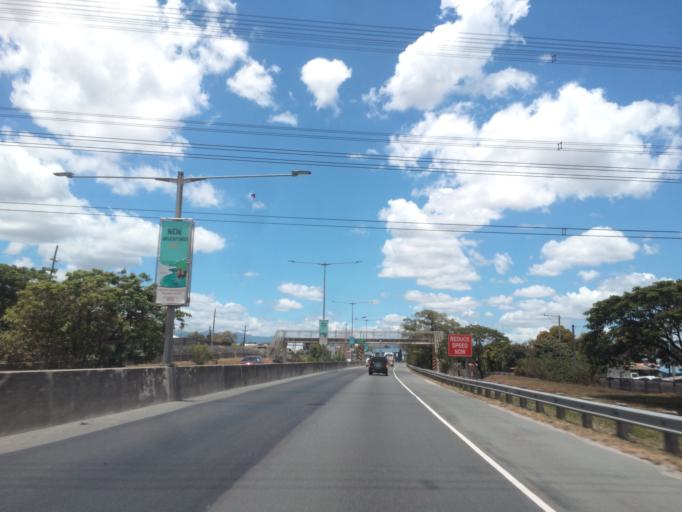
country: PH
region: Calabarzon
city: Bagong Pagasa
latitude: 14.6934
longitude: 121.0129
